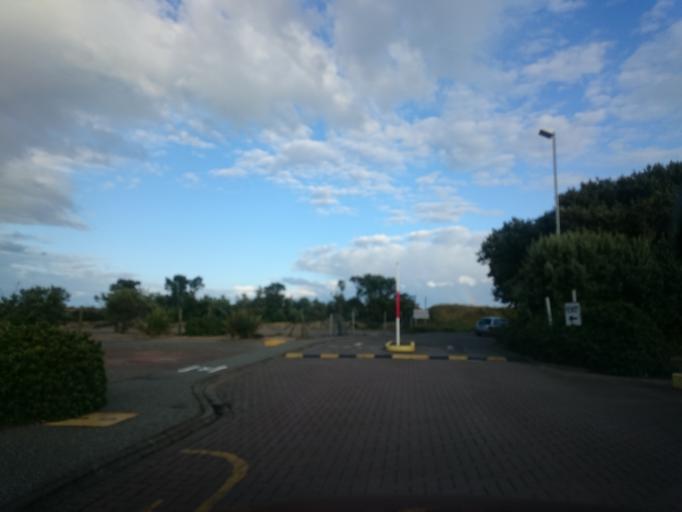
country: IE
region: Leinster
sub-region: Loch Garman
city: Ballygerry
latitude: 52.2520
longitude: -6.3333
